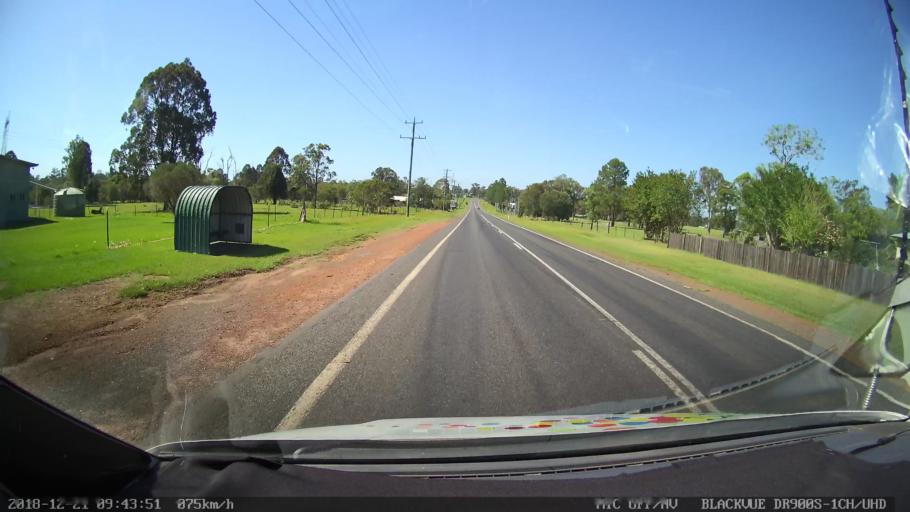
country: AU
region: New South Wales
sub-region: Clarence Valley
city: Grafton
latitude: -29.6113
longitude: 152.9351
